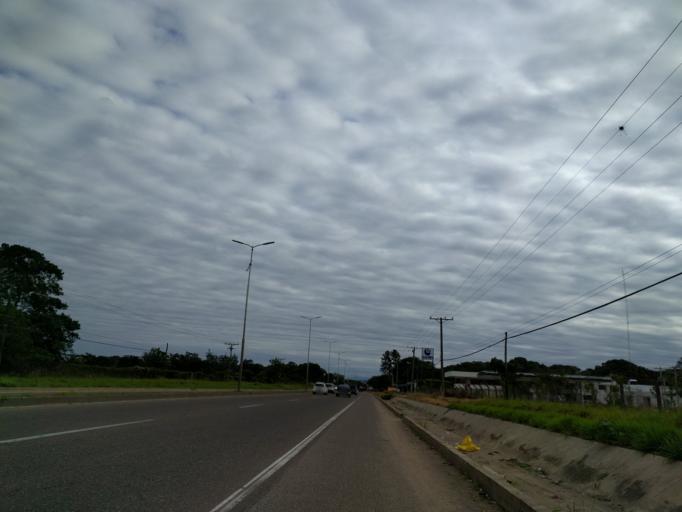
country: BO
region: Santa Cruz
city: Santa Cruz de la Sierra
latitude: -17.8592
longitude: -63.2619
